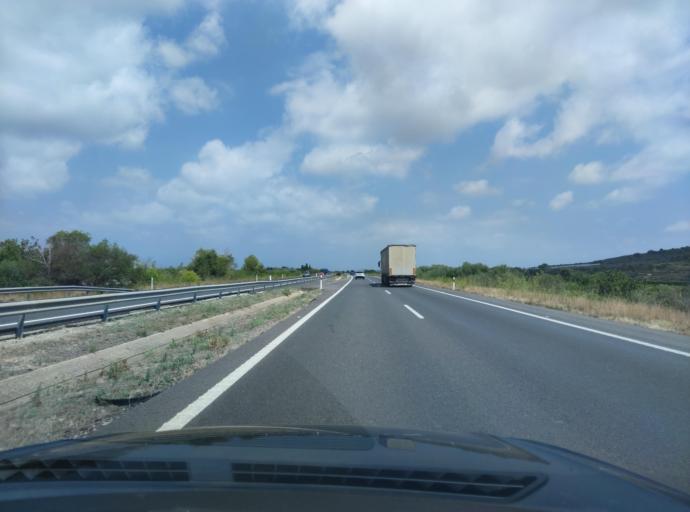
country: ES
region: Valencia
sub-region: Provincia de Castello
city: Vinaros
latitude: 40.5032
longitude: 0.4158
